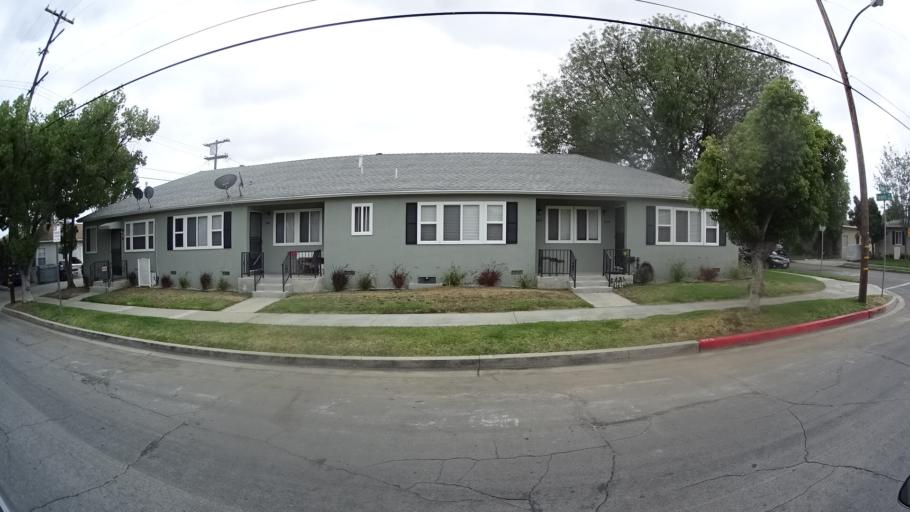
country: US
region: California
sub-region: Los Angeles County
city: Burbank
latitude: 34.2028
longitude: -118.3386
